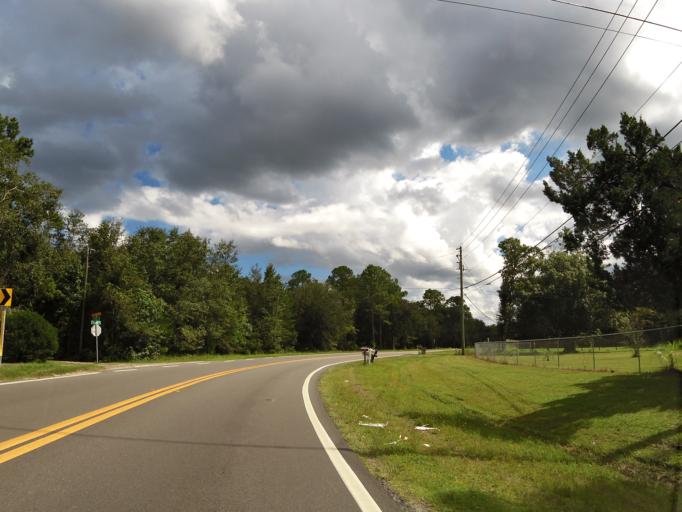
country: US
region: Florida
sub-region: Saint Johns County
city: Saint Augustine
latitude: 29.9412
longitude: -81.4945
